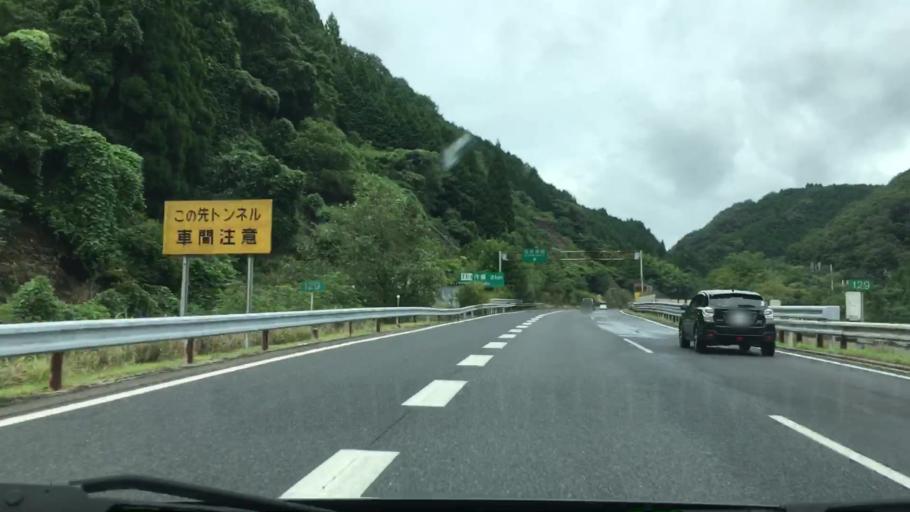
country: JP
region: Hyogo
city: Yamazakicho-nakabirose
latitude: 35.0137
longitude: 134.2734
